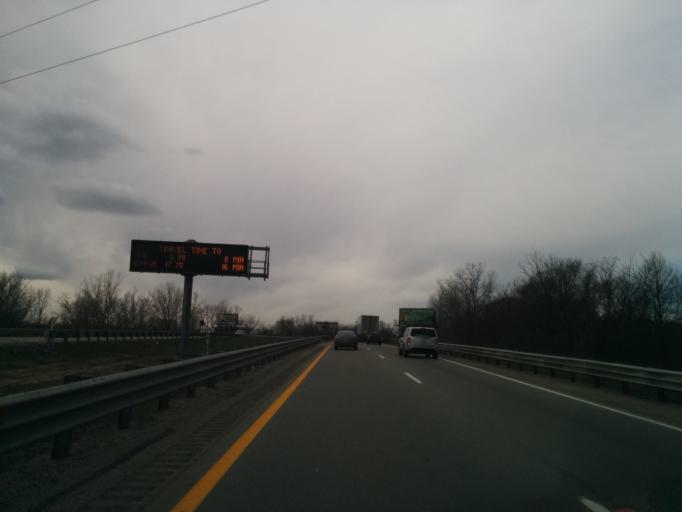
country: US
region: Michigan
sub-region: Kent County
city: Wyoming
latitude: 42.9359
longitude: -85.7215
